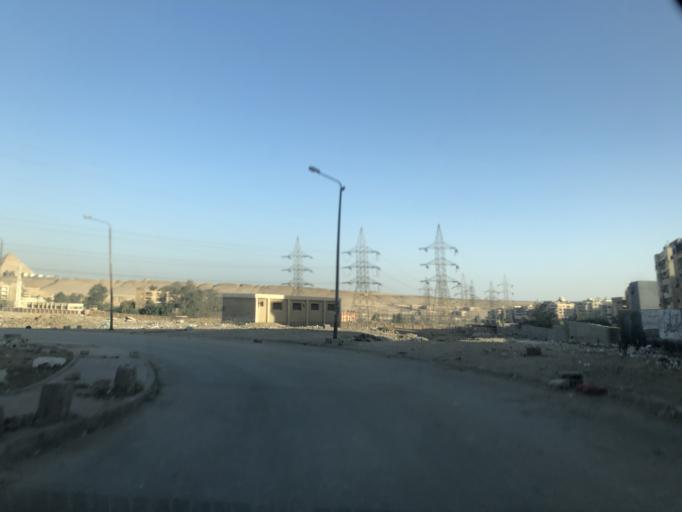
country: EG
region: Al Jizah
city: Al Jizah
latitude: 29.9845
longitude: 31.1089
